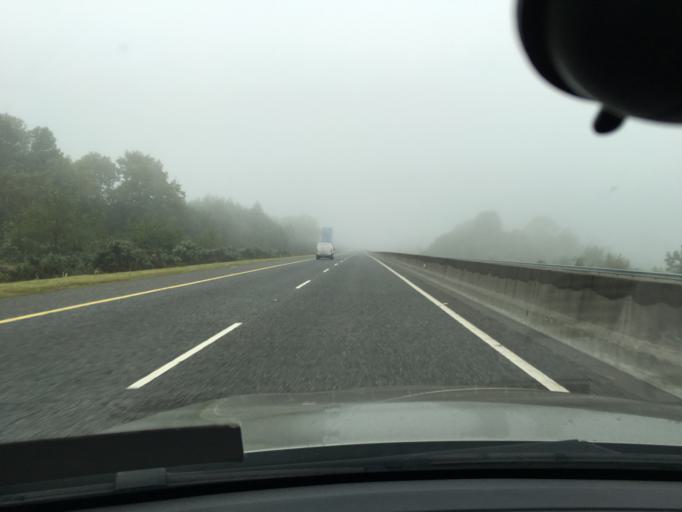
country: IE
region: Leinster
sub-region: An Iarmhi
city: Moate
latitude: 53.3907
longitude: -7.6555
